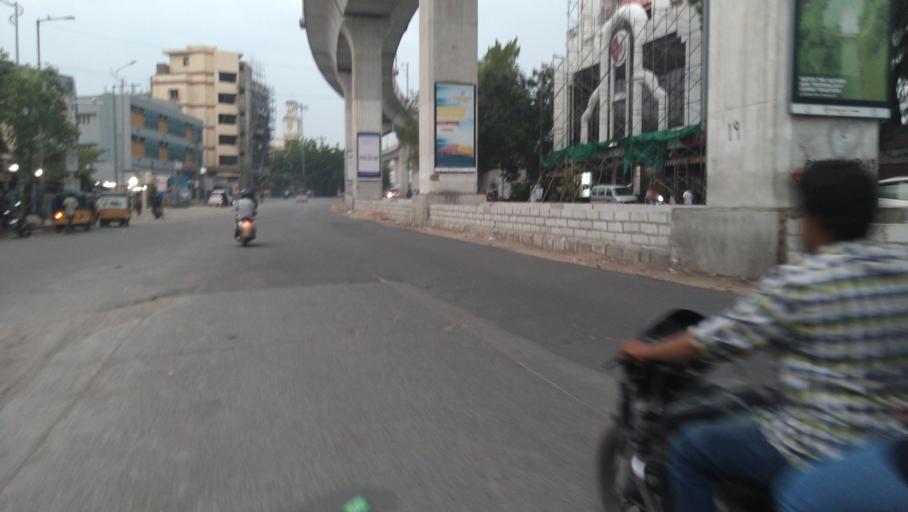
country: IN
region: Telangana
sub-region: Hyderabad
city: Malkajgiri
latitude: 17.4392
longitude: 78.4991
